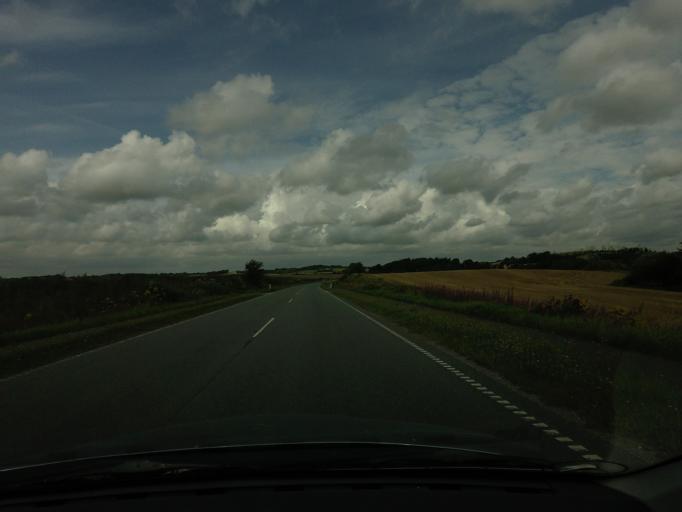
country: DK
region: North Denmark
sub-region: Hjorring Kommune
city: Tars
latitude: 57.3685
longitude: 10.1794
